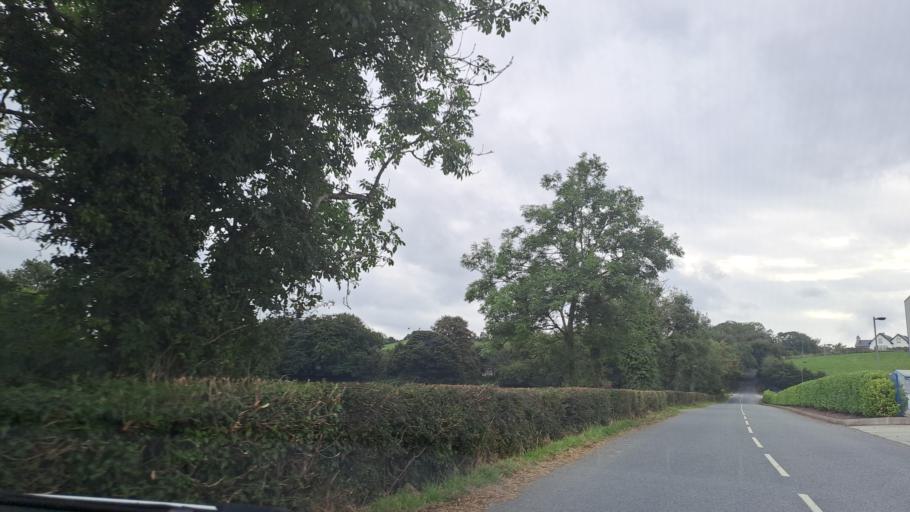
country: IE
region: Ulster
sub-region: An Cabhan
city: Kingscourt
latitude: 53.9958
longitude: -6.8538
